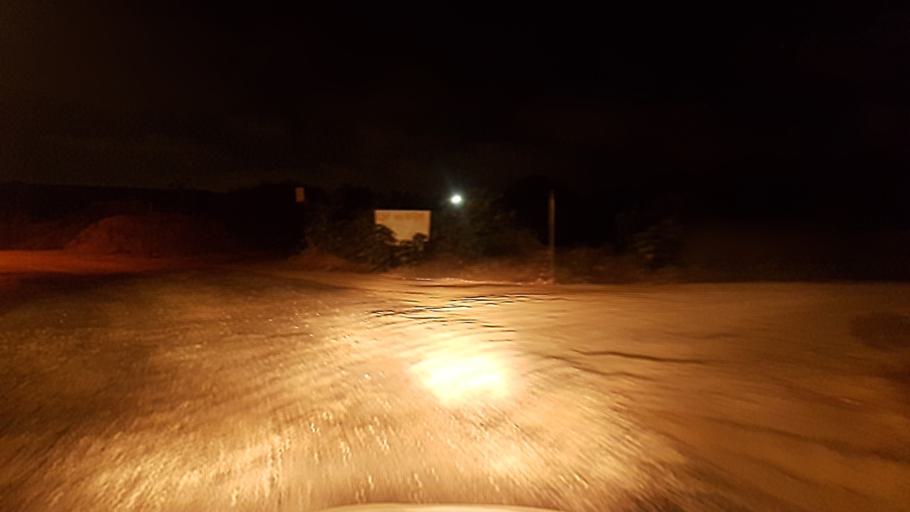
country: IL
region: Central District
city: Hod HaSharon
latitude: 32.1614
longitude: 34.8722
